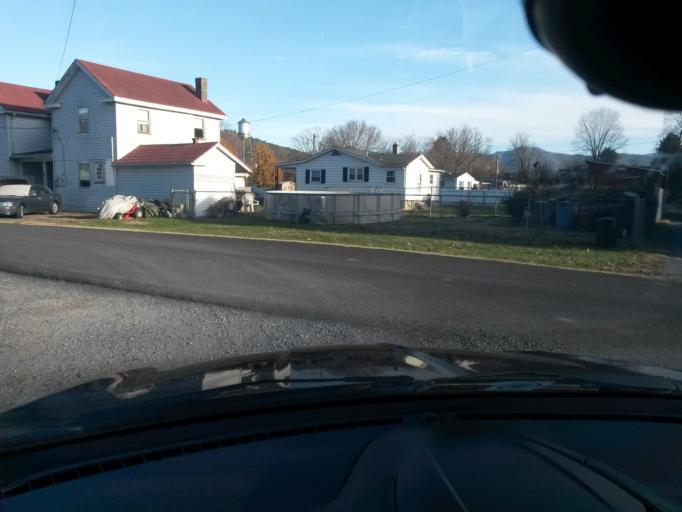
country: US
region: Virginia
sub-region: Alleghany County
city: Clifton Forge
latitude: 37.7981
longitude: -79.7909
